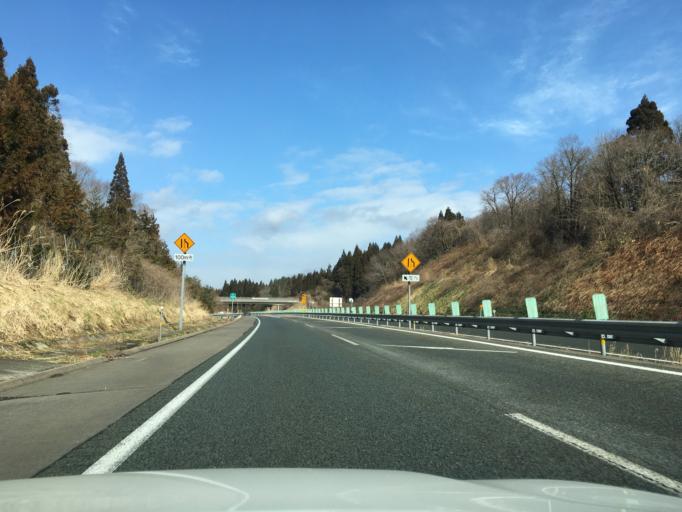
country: JP
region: Akita
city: Akita
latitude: 39.7266
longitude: 140.1806
